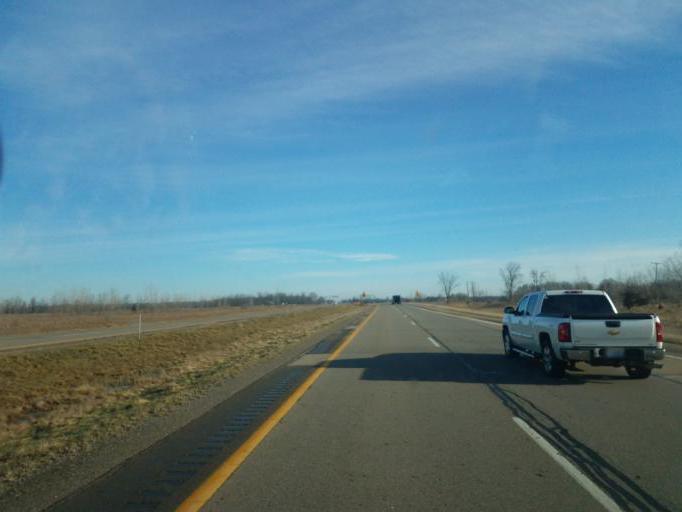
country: US
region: Michigan
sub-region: Gratiot County
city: Ithaca
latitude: 43.1794
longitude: -84.5634
